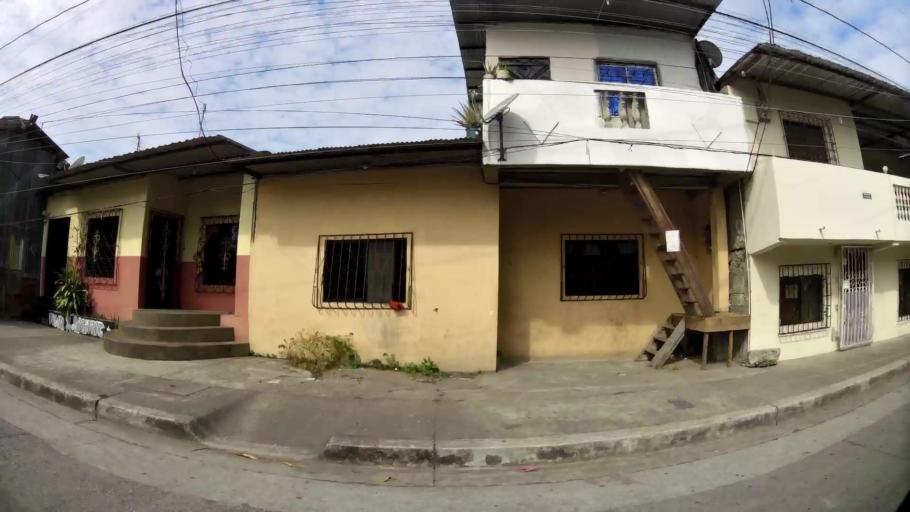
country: EC
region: Guayas
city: Guayaquil
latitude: -2.2592
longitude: -79.8746
